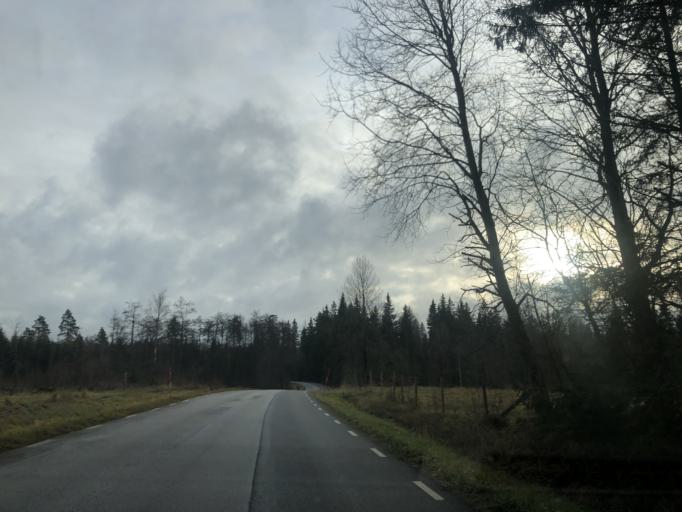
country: SE
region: Vaestra Goetaland
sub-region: Boras Kommun
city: Dalsjofors
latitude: 57.8187
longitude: 13.1966
